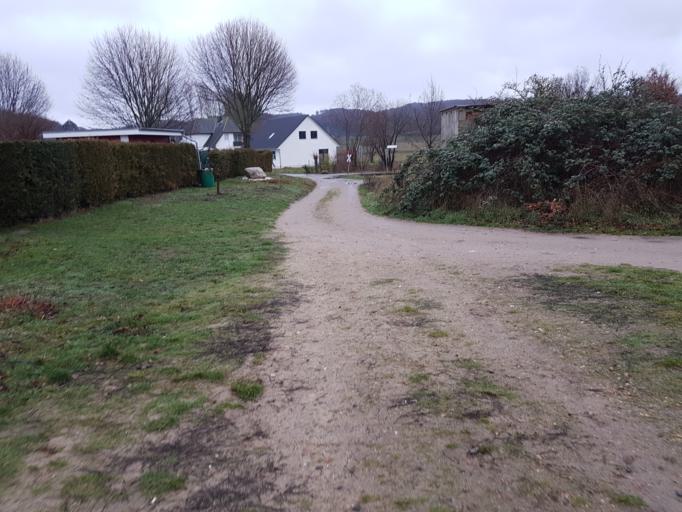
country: DE
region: Mecklenburg-Vorpommern
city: Ostseebad Binz
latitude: 54.3920
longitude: 13.6046
